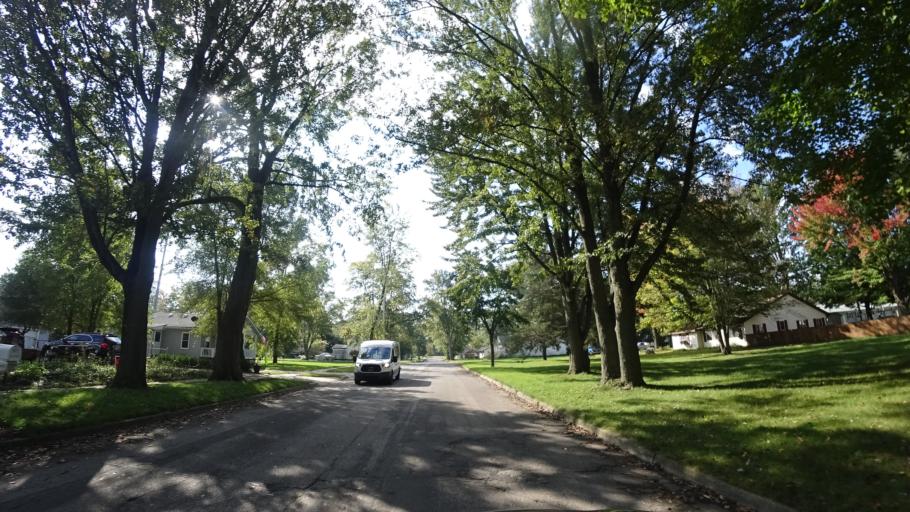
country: US
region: Michigan
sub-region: Saint Joseph County
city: Three Rivers
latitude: 41.9346
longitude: -85.6412
